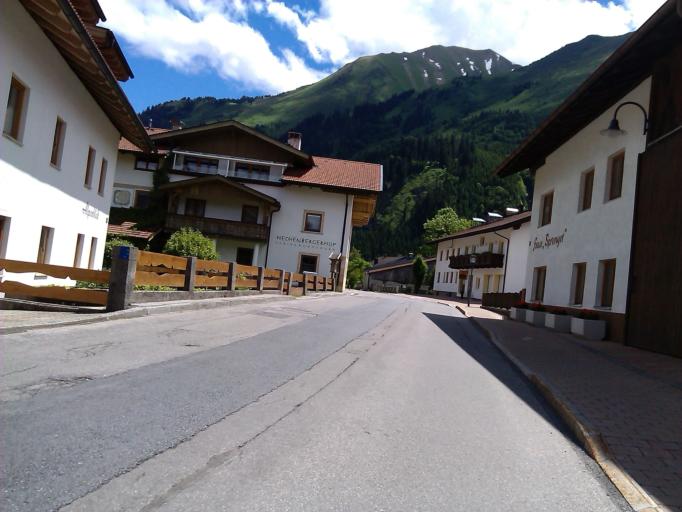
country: AT
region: Tyrol
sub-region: Politischer Bezirk Reutte
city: Bichlbach
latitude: 47.4192
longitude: 10.7918
